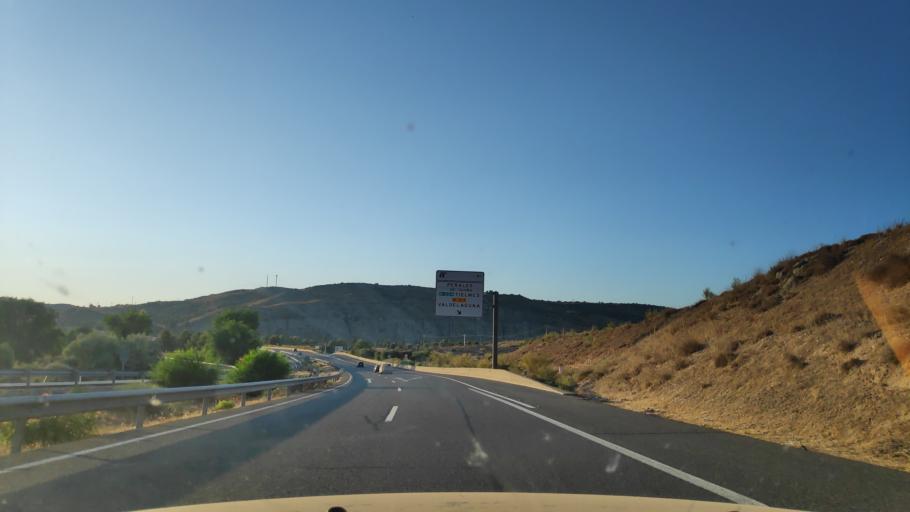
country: ES
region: Madrid
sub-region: Provincia de Madrid
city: Perales de Tajuna
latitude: 40.2211
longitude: -3.3302
